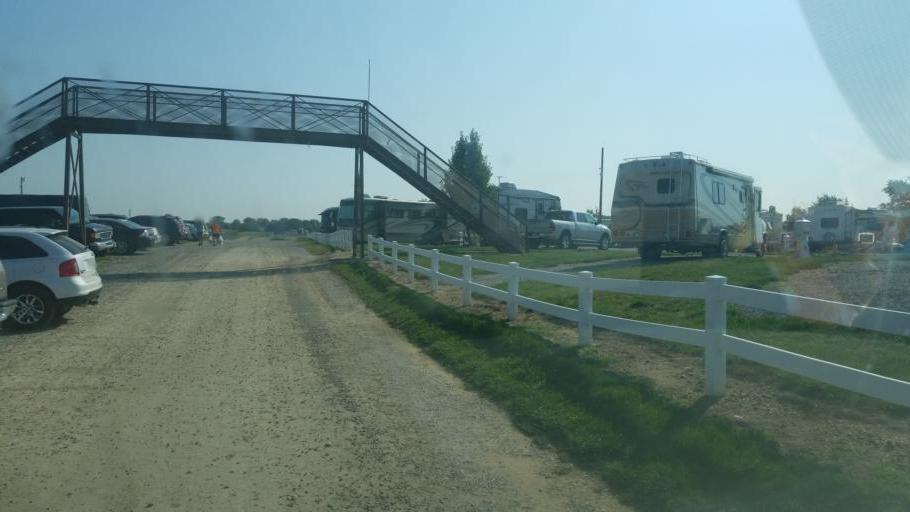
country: US
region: Indiana
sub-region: Elkhart County
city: Middlebury
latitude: 41.6706
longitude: -85.5779
